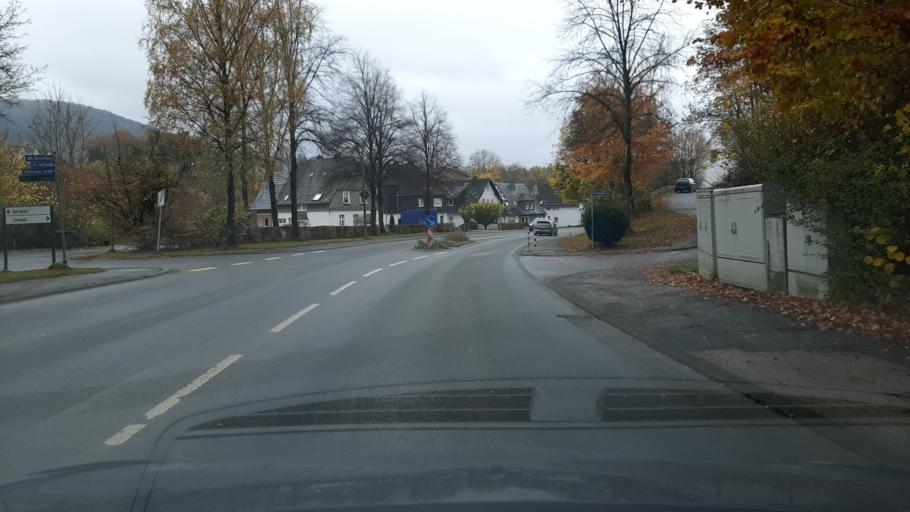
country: DE
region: North Rhine-Westphalia
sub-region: Regierungsbezirk Arnsberg
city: Bad Fredeburg
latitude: 51.1672
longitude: 8.3160
